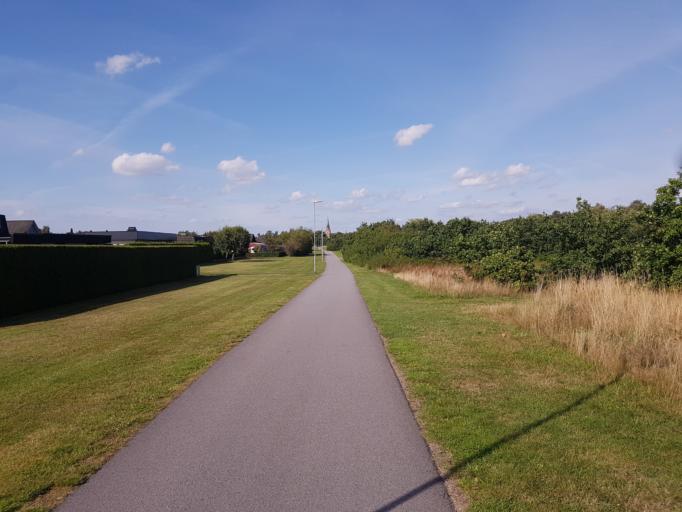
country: SE
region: Skane
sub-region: Sjobo Kommun
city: Sjoebo
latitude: 55.6380
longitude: 13.6994
